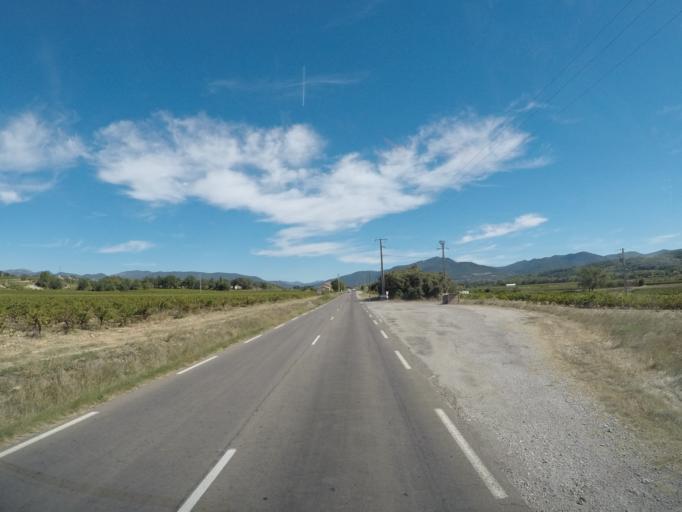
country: FR
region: Rhone-Alpes
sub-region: Departement de la Drome
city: Vinsobres
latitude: 44.3132
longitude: 5.0493
